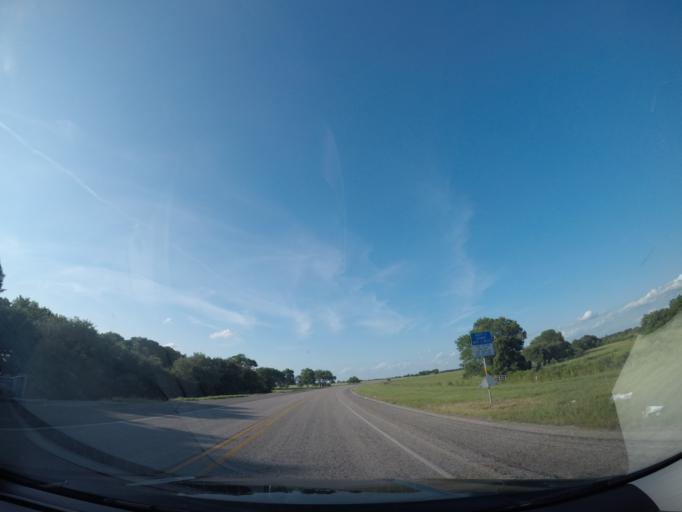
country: US
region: Texas
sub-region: Austin County
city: Wallis
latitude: 29.6038
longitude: -96.0894
